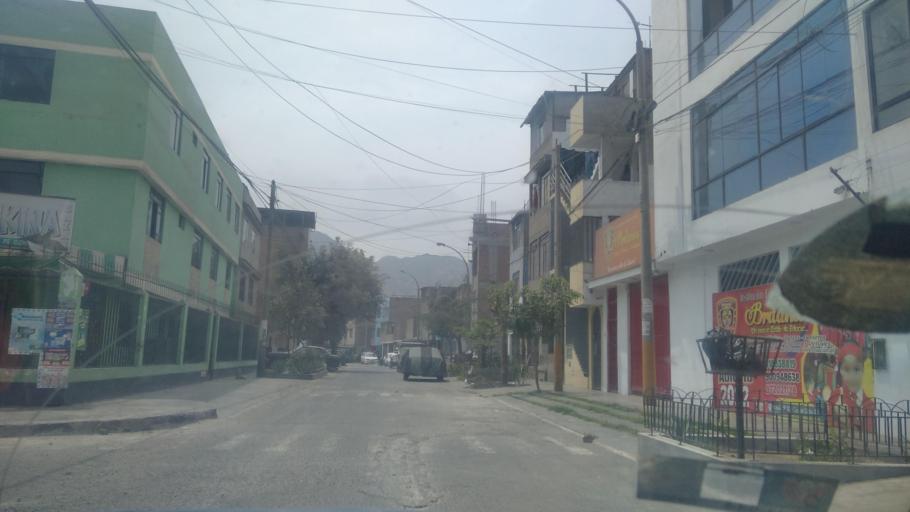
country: PE
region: Lima
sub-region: Lima
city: Independencia
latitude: -11.9857
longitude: -77.0086
